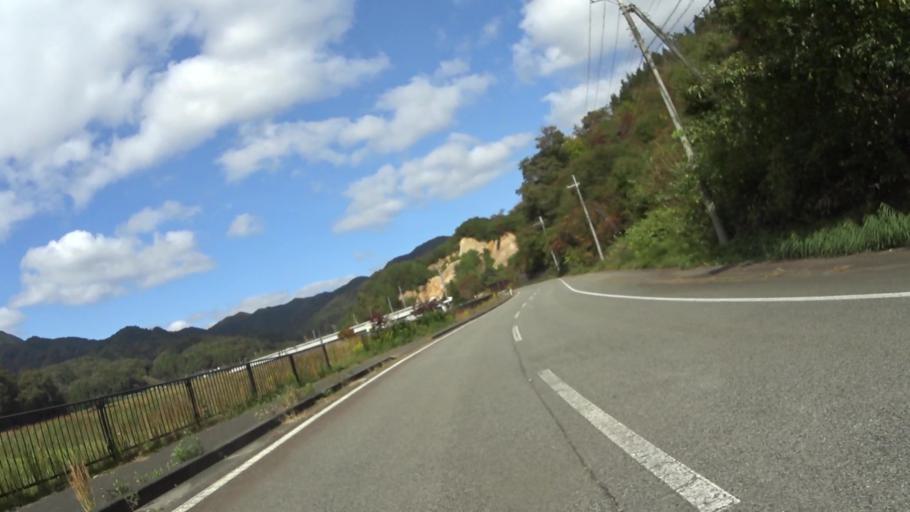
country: JP
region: Hyogo
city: Toyooka
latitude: 35.5014
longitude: 134.9925
